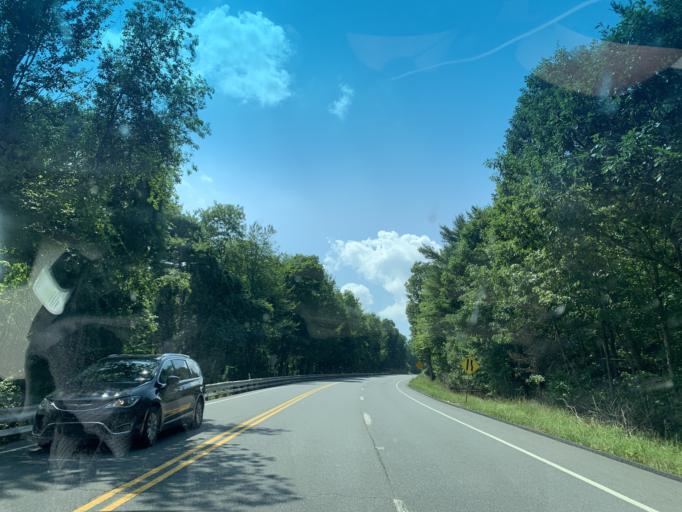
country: US
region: Pennsylvania
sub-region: Schuylkill County
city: Frackville
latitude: 40.7808
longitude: -76.2506
